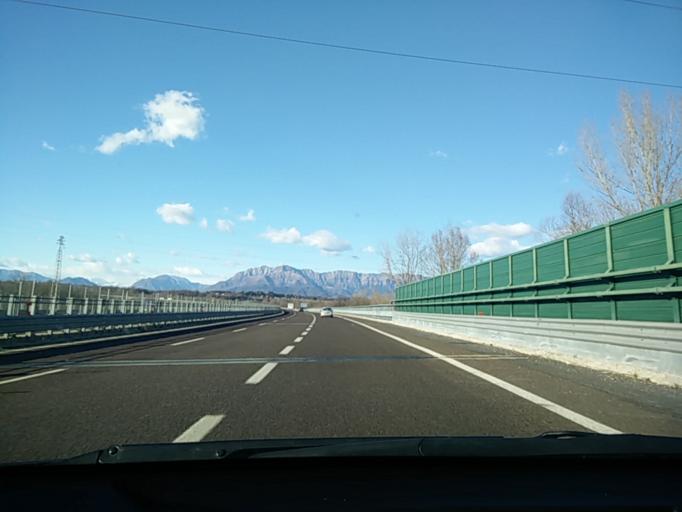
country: IT
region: Friuli Venezia Giulia
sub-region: Provincia di Udine
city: Tavagnacco
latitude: 46.1165
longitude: 13.2056
